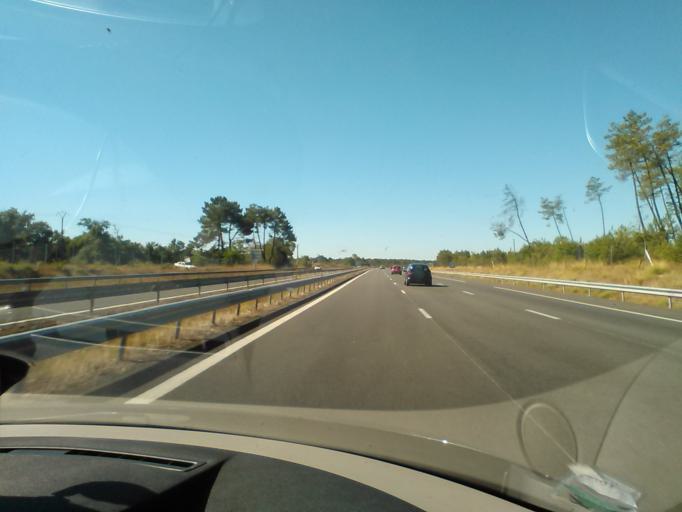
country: FR
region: Aquitaine
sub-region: Departement des Landes
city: Labouheyre
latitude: 44.1444
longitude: -0.9699
